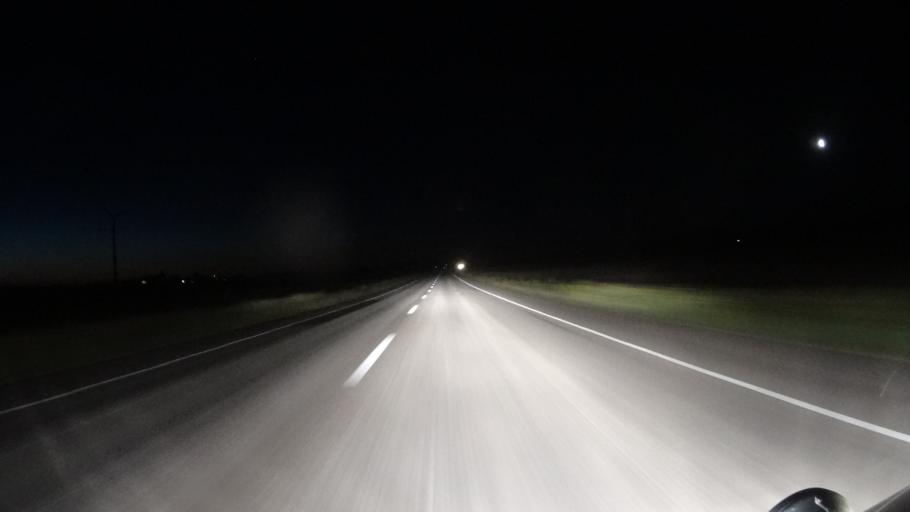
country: SE
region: OEstergoetland
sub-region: Vadstena Kommun
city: Herrestad
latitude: 58.2846
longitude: 14.7658
